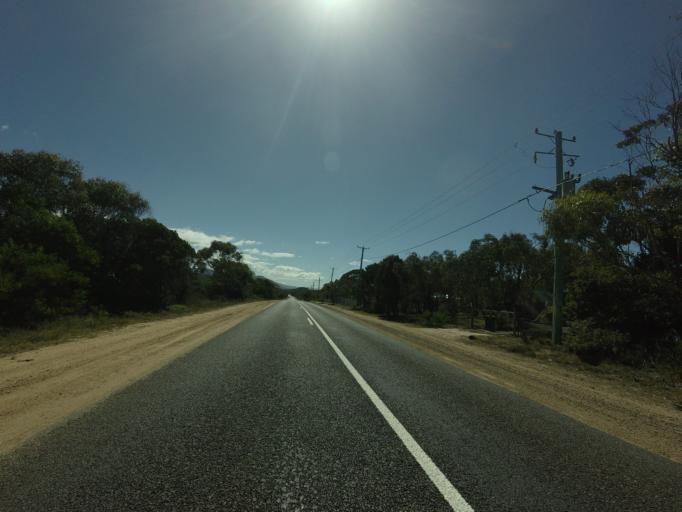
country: AU
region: Tasmania
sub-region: Break O'Day
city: St Helens
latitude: -41.8186
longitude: 148.2627
